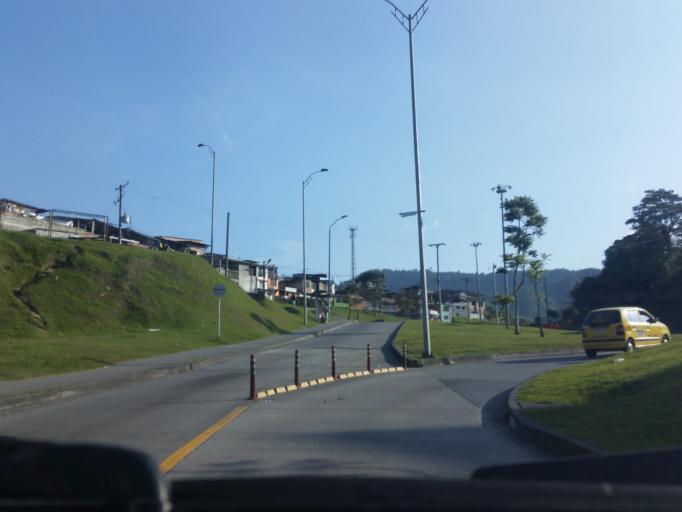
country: CO
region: Caldas
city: Manizales
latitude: 5.0713
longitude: -75.4951
